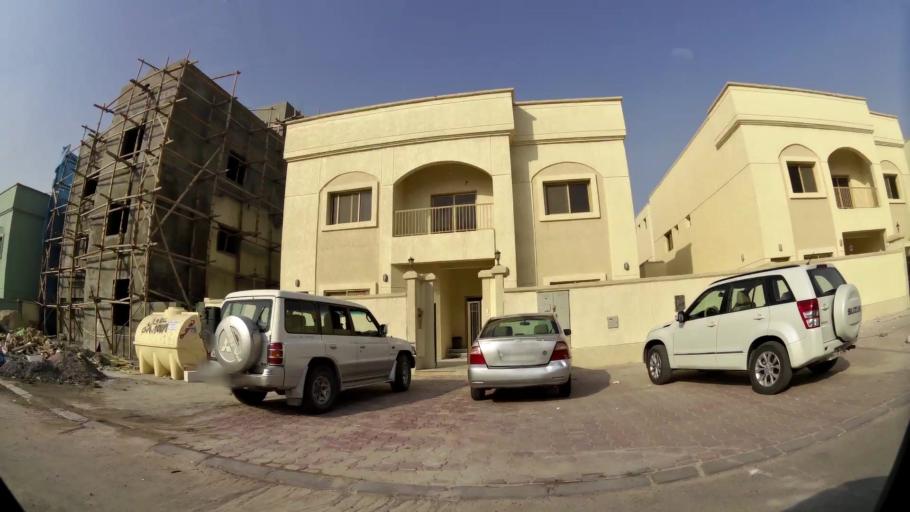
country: KW
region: Al Asimah
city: Ar Rabiyah
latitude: 29.3339
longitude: 47.8046
